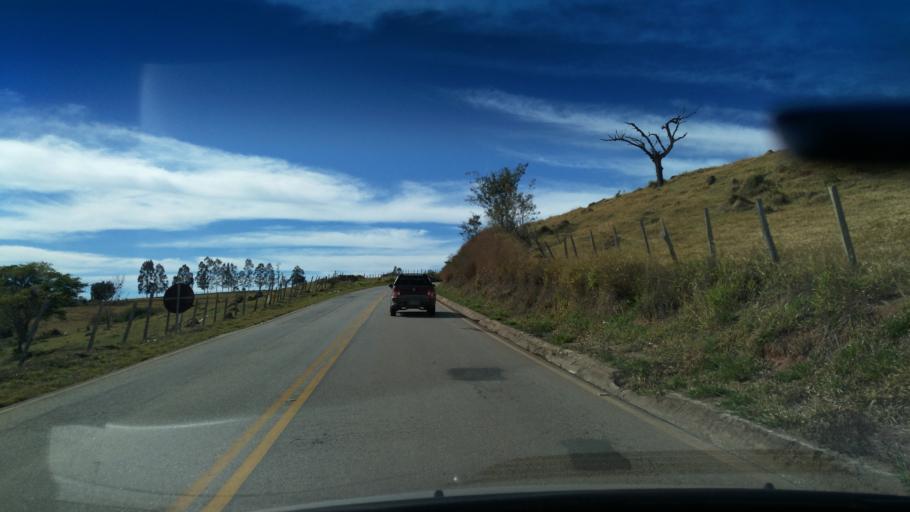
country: BR
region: Minas Gerais
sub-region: Andradas
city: Andradas
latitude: -22.0675
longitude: -46.4574
